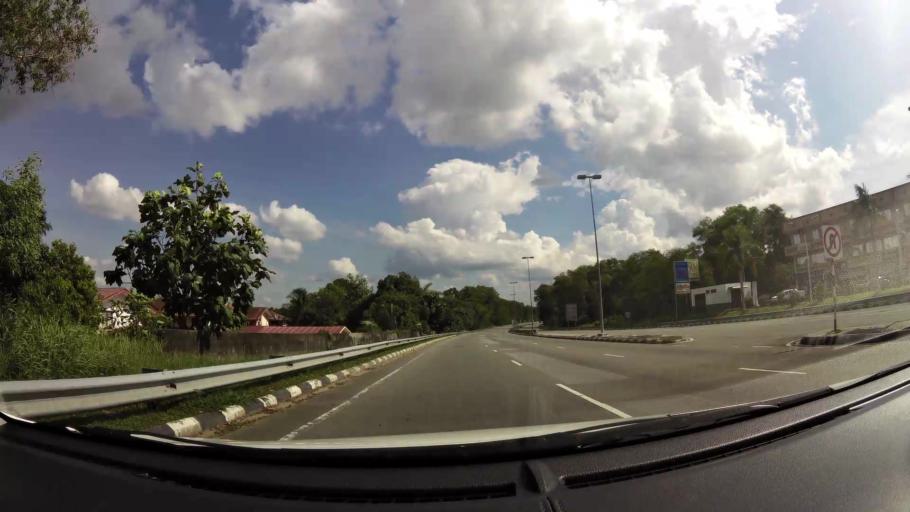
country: BN
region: Brunei and Muara
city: Bandar Seri Begawan
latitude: 4.9623
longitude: 114.9520
